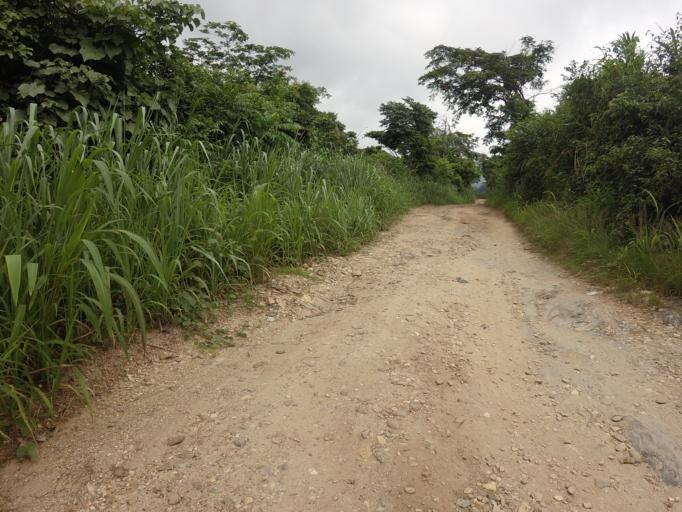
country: TG
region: Plateaux
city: Kpalime
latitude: 6.8736
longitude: 0.4426
